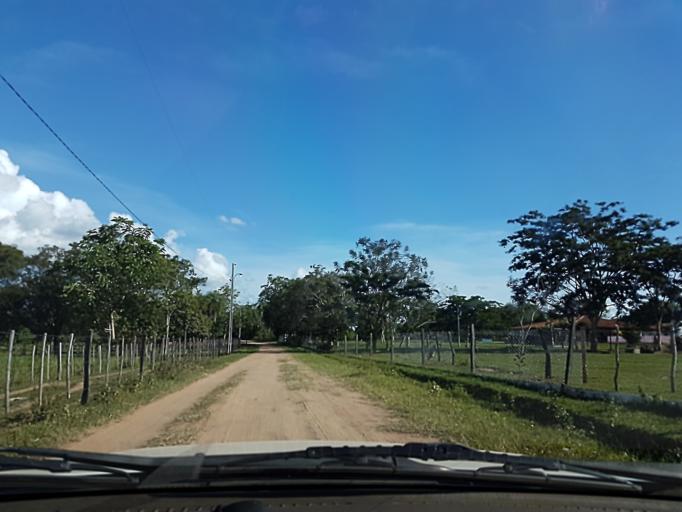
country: PY
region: Cordillera
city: Arroyos y Esteros
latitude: -24.9846
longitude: -57.1996
